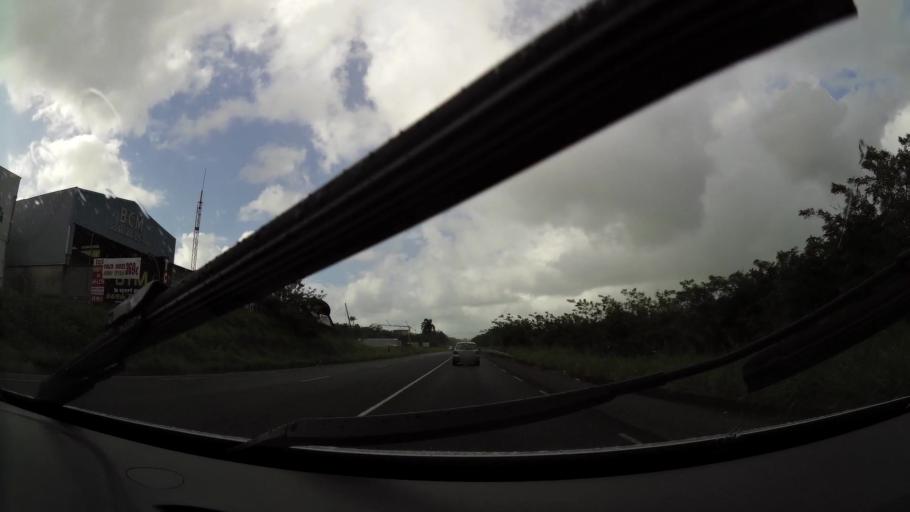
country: MQ
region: Martinique
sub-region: Martinique
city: Sainte-Luce
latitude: 14.4965
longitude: -60.9763
